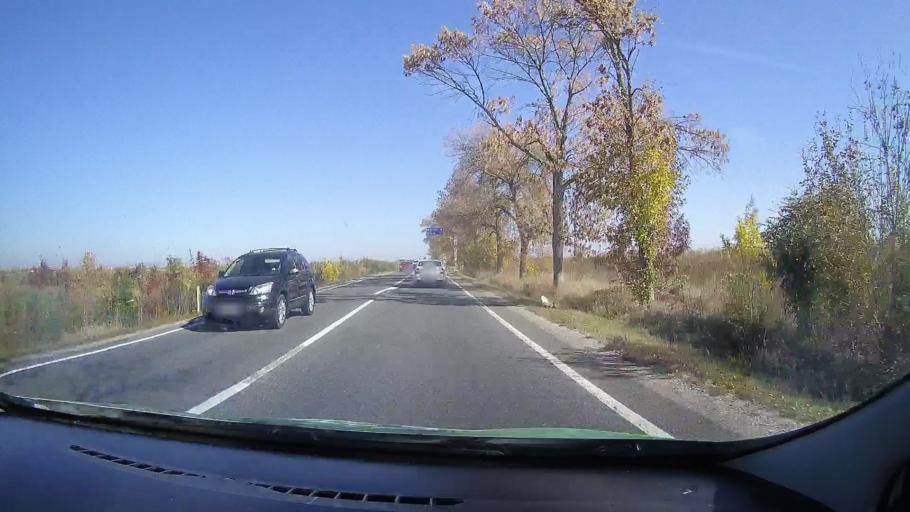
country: RO
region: Satu Mare
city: Moftinu Mare
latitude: 47.7163
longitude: 22.6525
